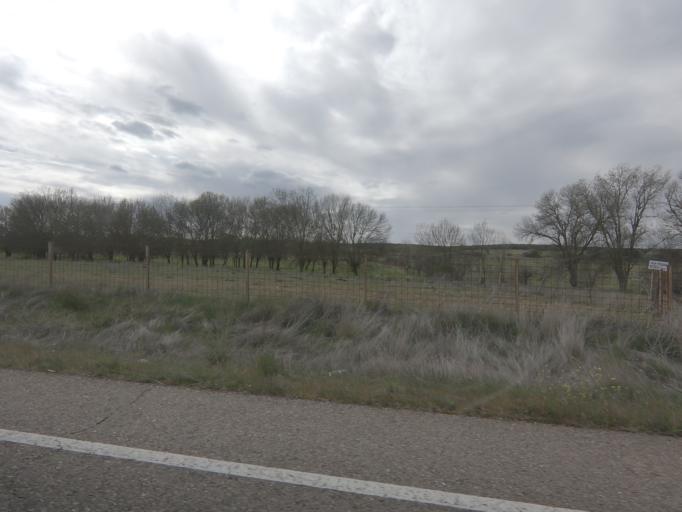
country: ES
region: Castille and Leon
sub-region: Provincia de Salamanca
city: Pastores
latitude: 40.5400
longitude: -6.5648
